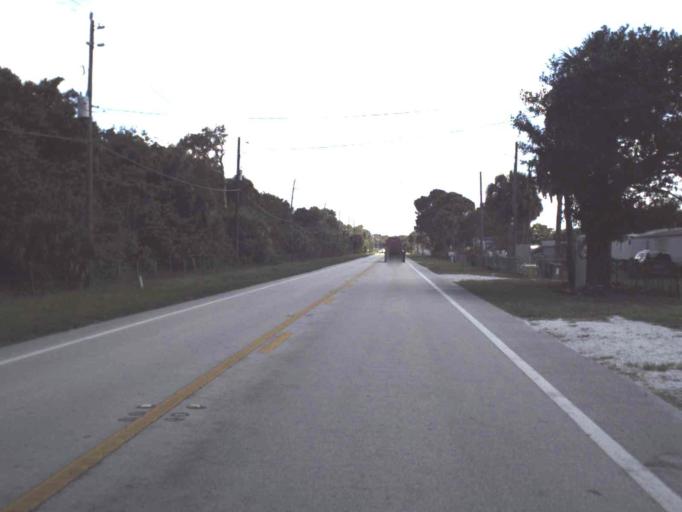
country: US
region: Florida
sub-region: Okeechobee County
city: Taylor Creek
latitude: 27.1900
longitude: -80.7519
